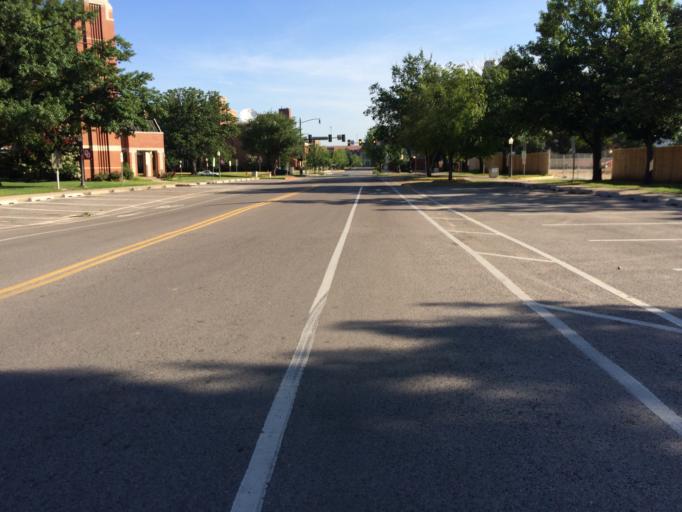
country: US
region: Oklahoma
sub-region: Cleveland County
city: Norman
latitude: 35.2028
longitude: -97.4442
